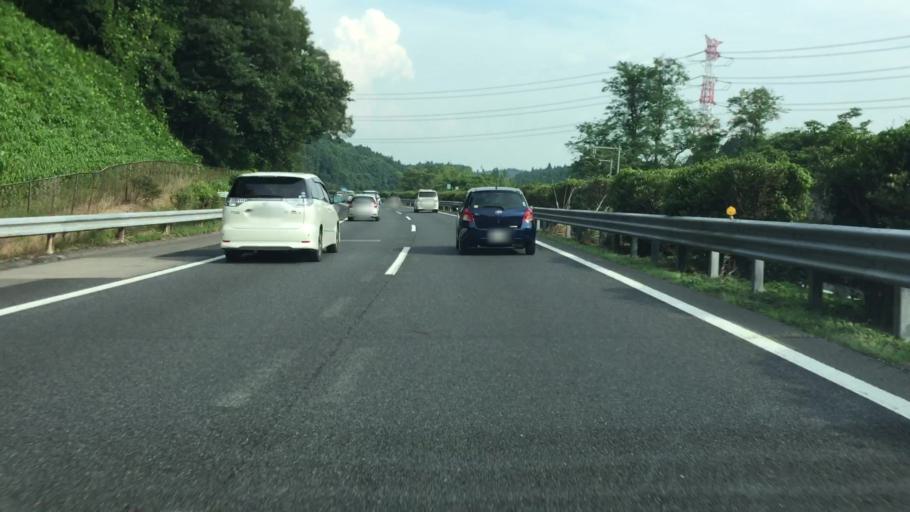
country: JP
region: Tochigi
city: Yaita
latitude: 36.7875
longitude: 139.9181
